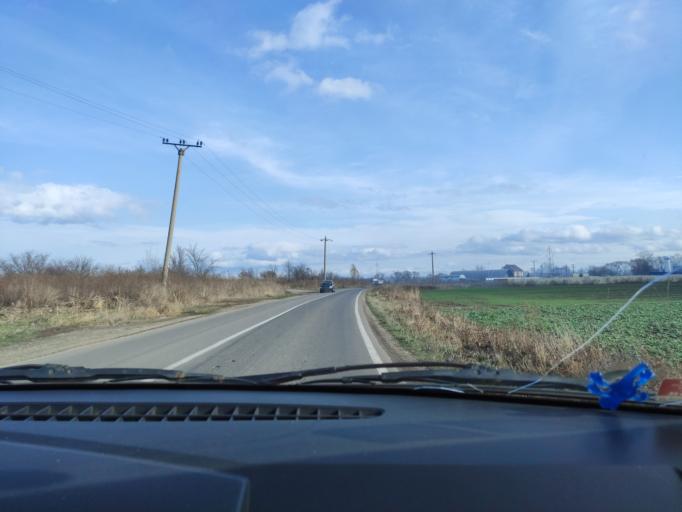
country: RO
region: Brasov
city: Codlea
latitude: 45.7155
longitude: 25.4697
